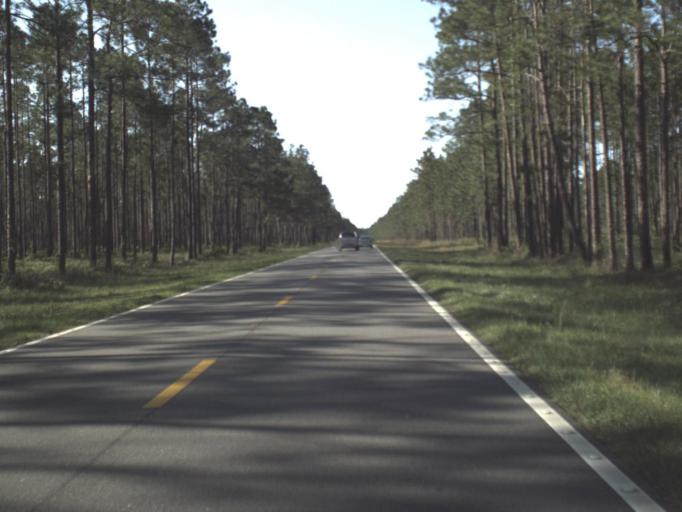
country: US
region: Florida
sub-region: Gulf County
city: Wewahitchka
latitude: 30.1150
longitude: -84.9876
